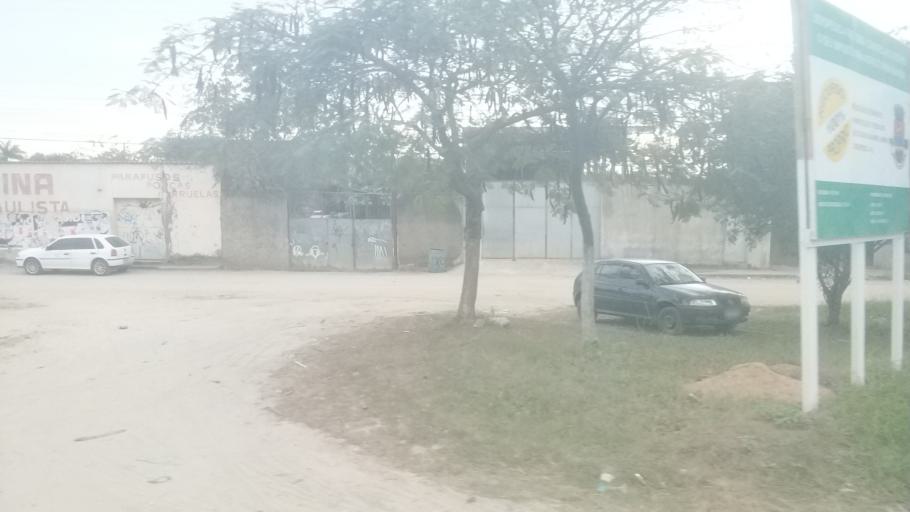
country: BR
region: Rio de Janeiro
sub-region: Seropedica
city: Seropedica
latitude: -22.8025
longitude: -43.6420
